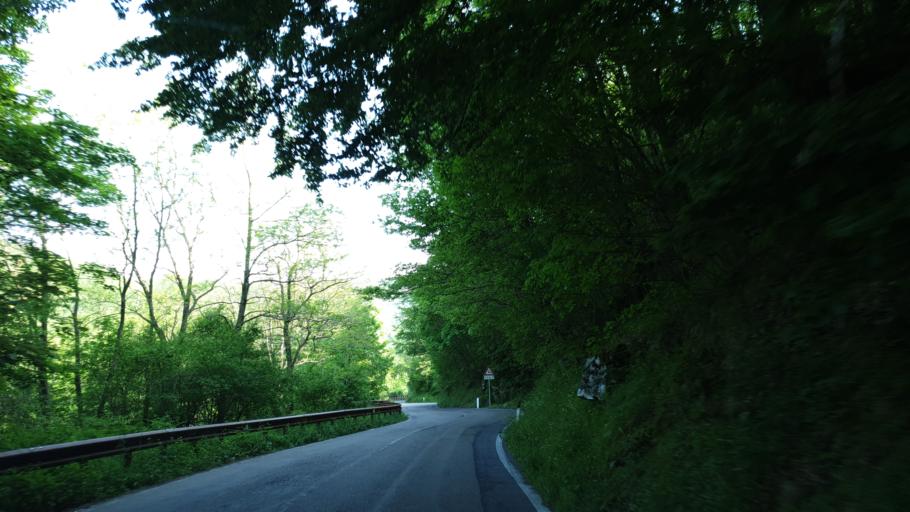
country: IT
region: Tuscany
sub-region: Province of Arezzo
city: Soci
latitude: 43.7840
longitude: 11.8685
